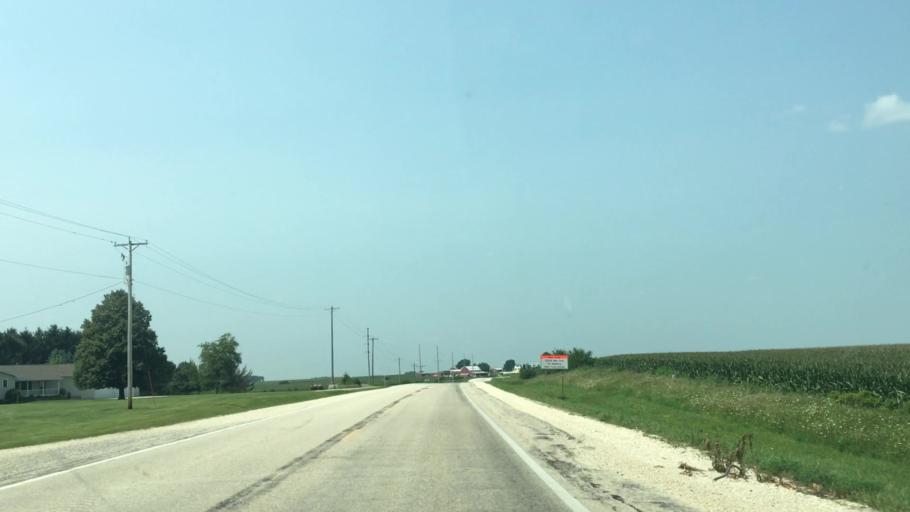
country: US
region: Iowa
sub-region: Fayette County
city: West Union
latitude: 42.9734
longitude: -91.8190
